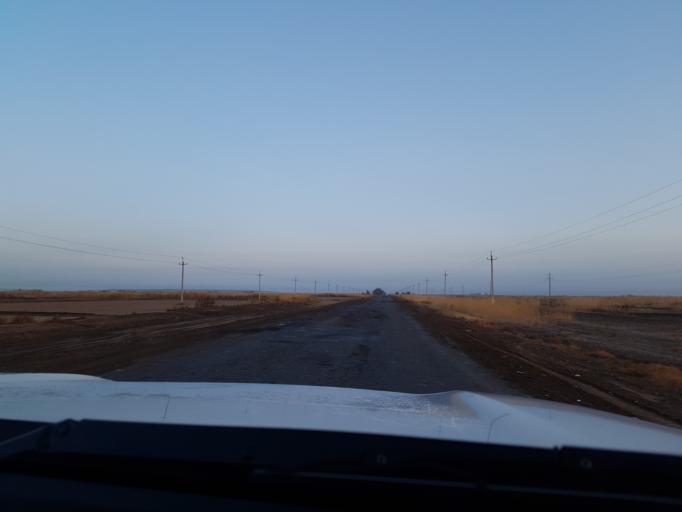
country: TM
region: Dasoguz
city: Koeneuergench
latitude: 41.7521
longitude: 58.6897
